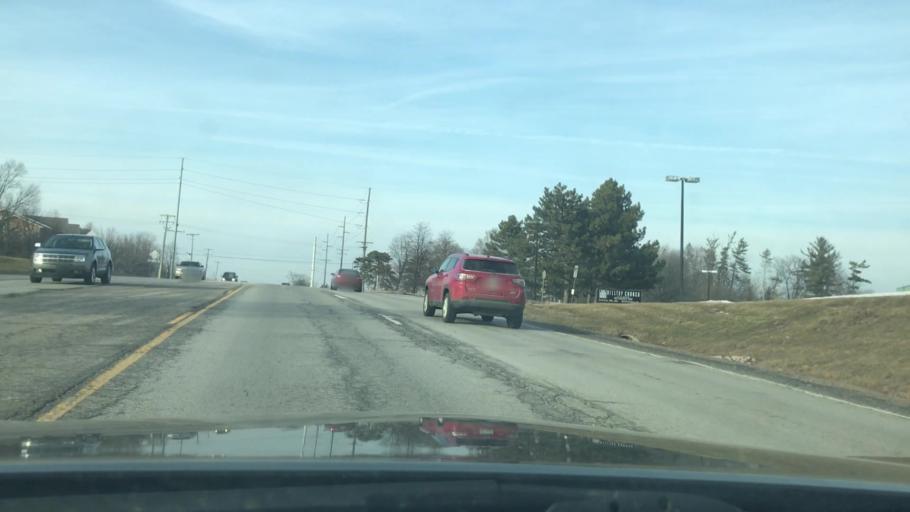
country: US
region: Michigan
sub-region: Wayne County
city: Northville
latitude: 42.4448
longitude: -83.4340
